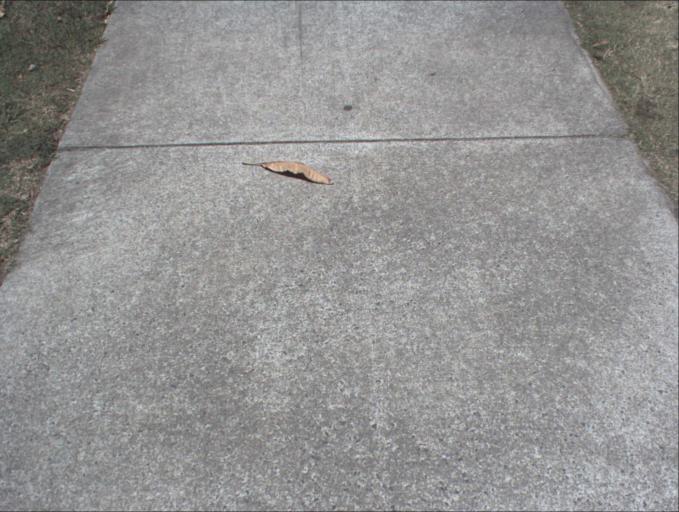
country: AU
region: Queensland
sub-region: Gold Coast
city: Yatala
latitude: -27.7095
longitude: 153.2119
